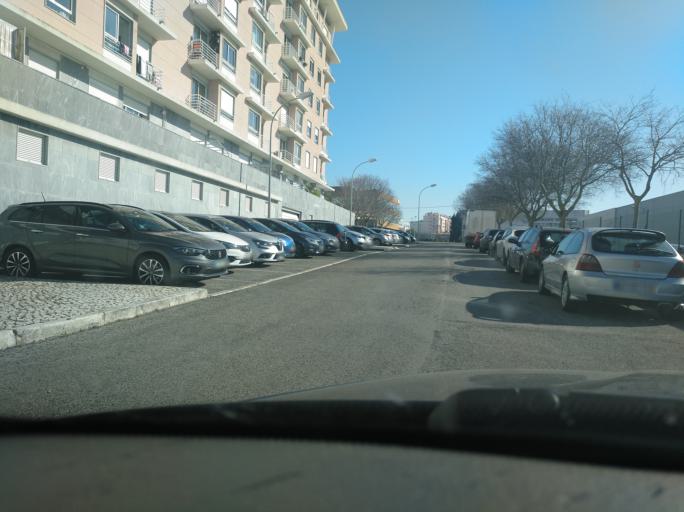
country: PT
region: Lisbon
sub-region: Odivelas
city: Pontinha
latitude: 38.7677
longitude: -9.1849
